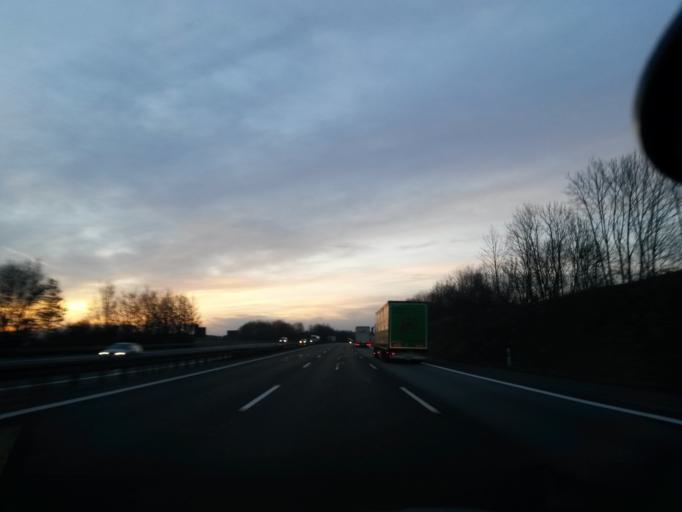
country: DE
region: Bavaria
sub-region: Upper Bavaria
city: Denkendorf
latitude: 48.9463
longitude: 11.4393
